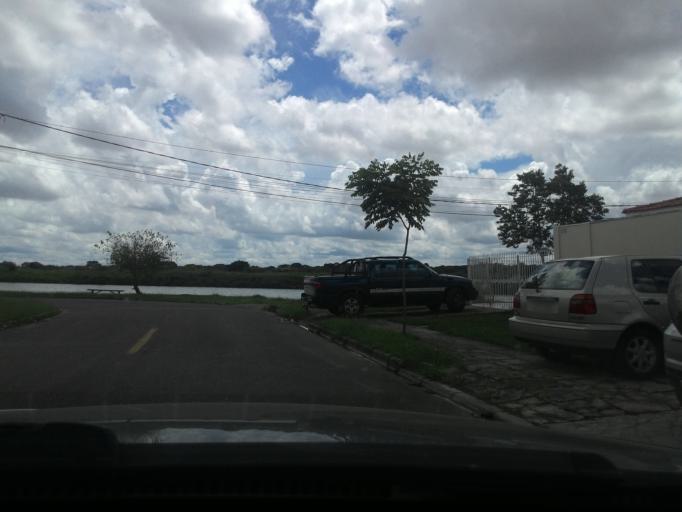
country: BR
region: Parana
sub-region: Sao Jose Dos Pinhais
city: Sao Jose dos Pinhais
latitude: -25.5045
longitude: -49.2083
